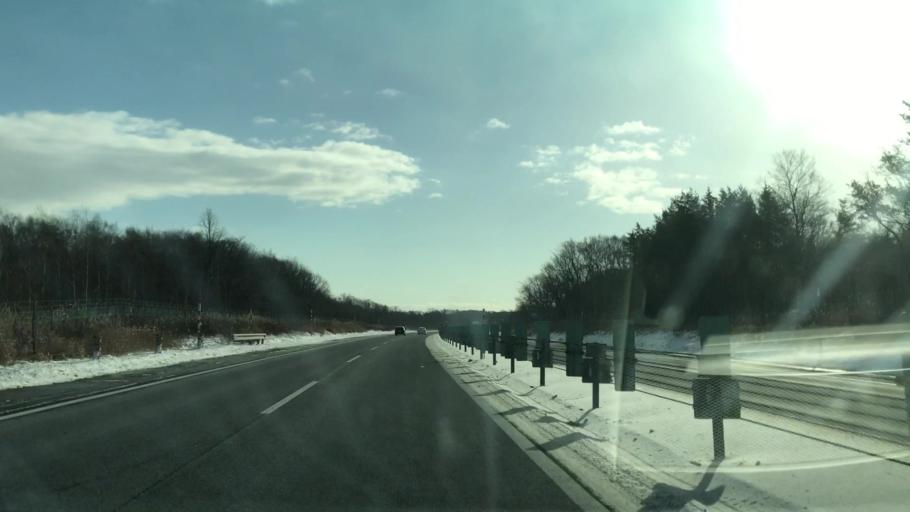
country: JP
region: Hokkaido
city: Chitose
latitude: 42.8389
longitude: 141.6020
